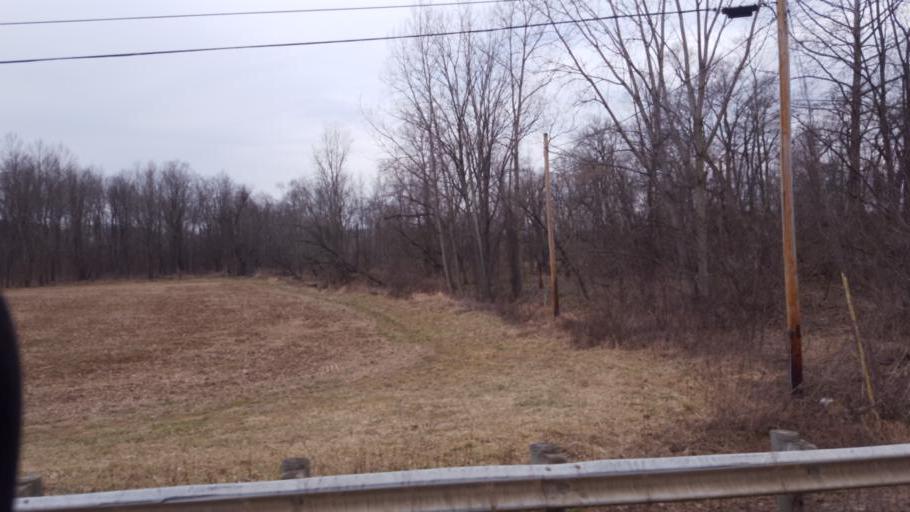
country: US
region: Ohio
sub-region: Ashland County
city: Loudonville
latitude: 40.6553
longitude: -82.2479
